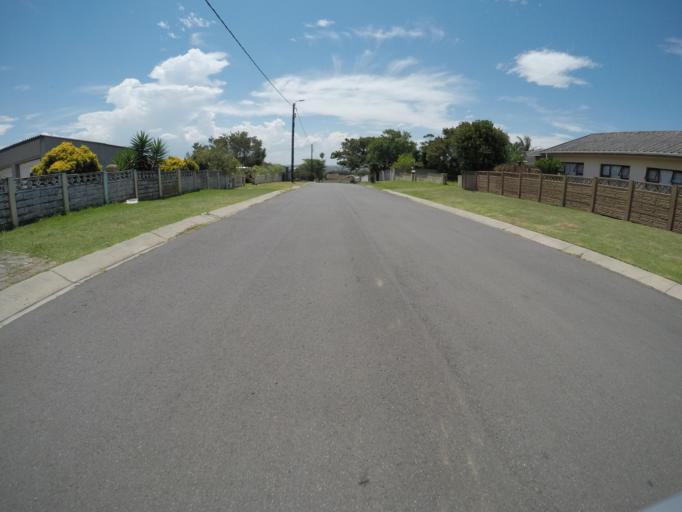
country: ZA
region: Eastern Cape
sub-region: Buffalo City Metropolitan Municipality
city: East London
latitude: -33.0336
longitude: 27.8508
